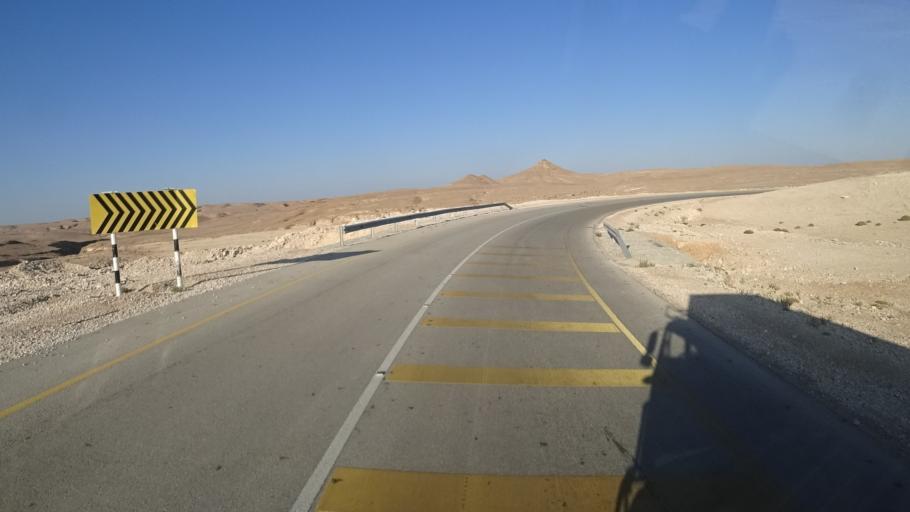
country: YE
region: Al Mahrah
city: Hawf
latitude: 17.0952
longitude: 53.0647
